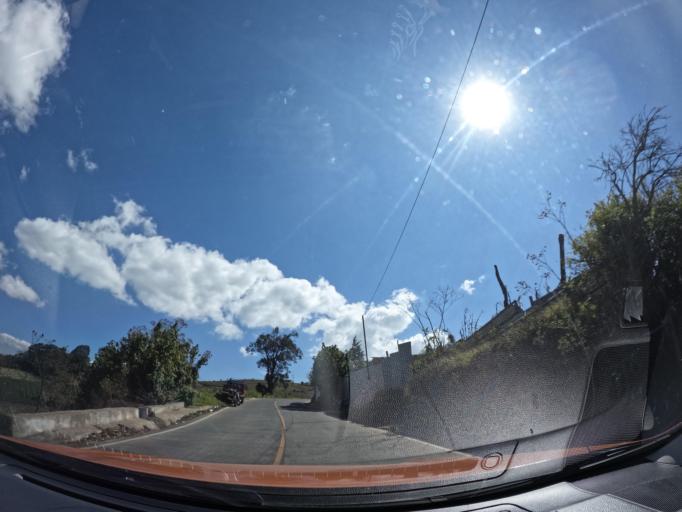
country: GT
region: Chimaltenango
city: Patzun
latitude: 14.6585
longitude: -91.0543
